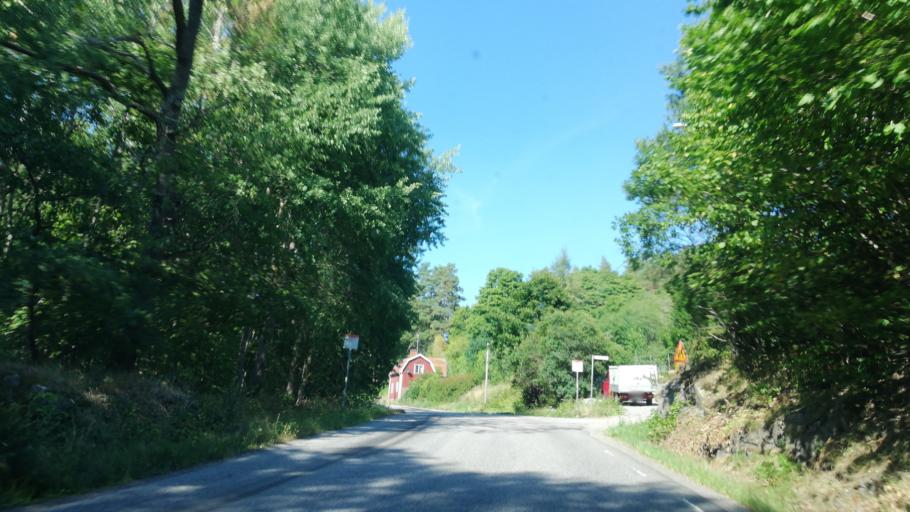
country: SE
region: OEstergoetland
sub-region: Finspangs Kommun
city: Finspang
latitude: 58.7227
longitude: 15.8323
